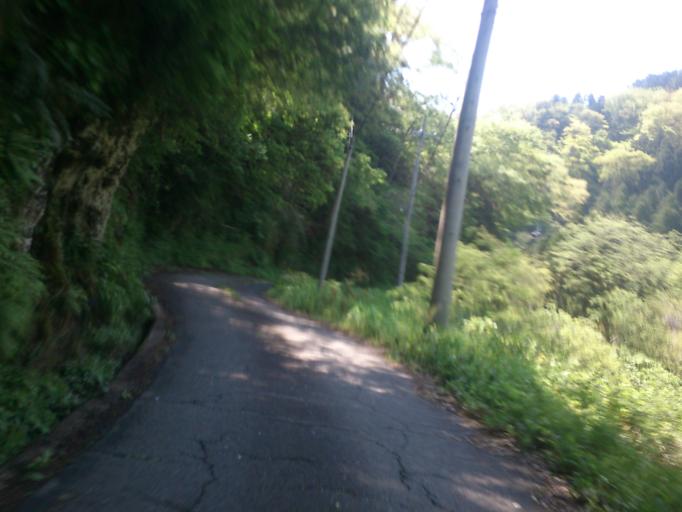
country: JP
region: Kyoto
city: Miyazu
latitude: 35.7220
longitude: 135.1618
